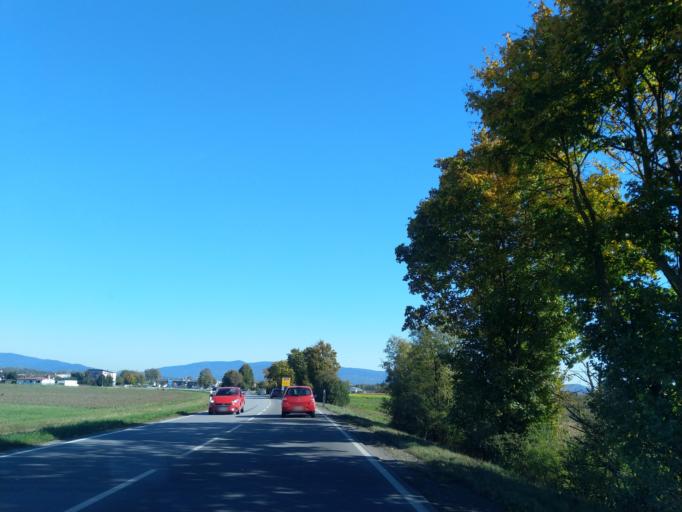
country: DE
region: Bavaria
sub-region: Lower Bavaria
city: Plattling
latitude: 48.7908
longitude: 12.9026
